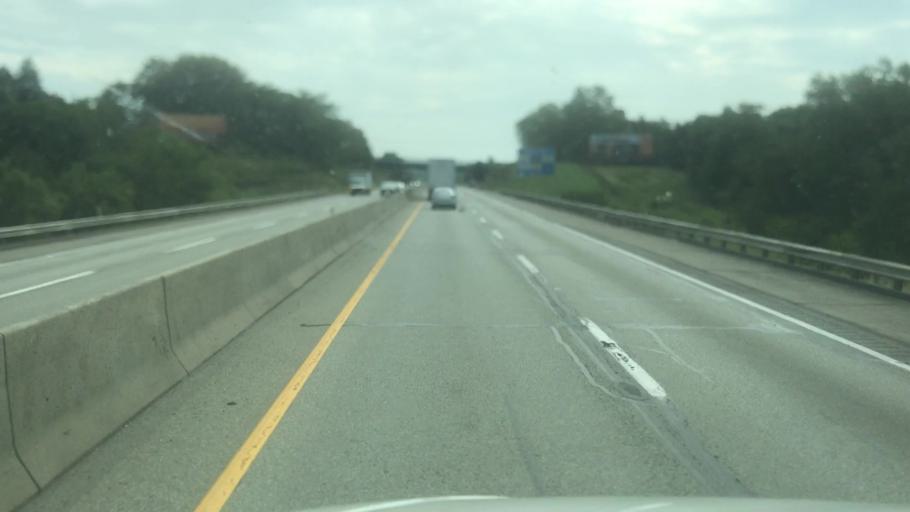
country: US
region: Pennsylvania
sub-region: Beaver County
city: Freedom
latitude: 40.7469
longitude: -80.2026
